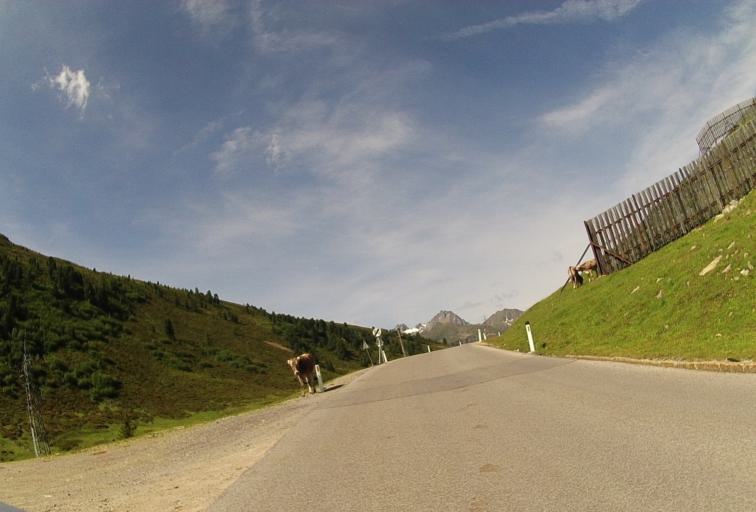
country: AT
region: Tyrol
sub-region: Politischer Bezirk Imst
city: Rietz
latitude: 47.2207
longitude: 11.0456
